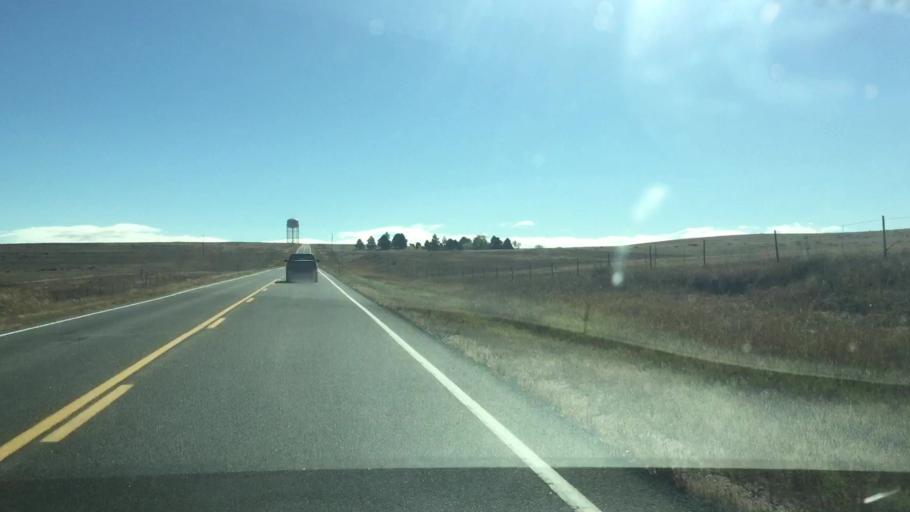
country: US
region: Colorado
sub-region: Elbert County
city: Kiowa
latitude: 39.3440
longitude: -104.4509
